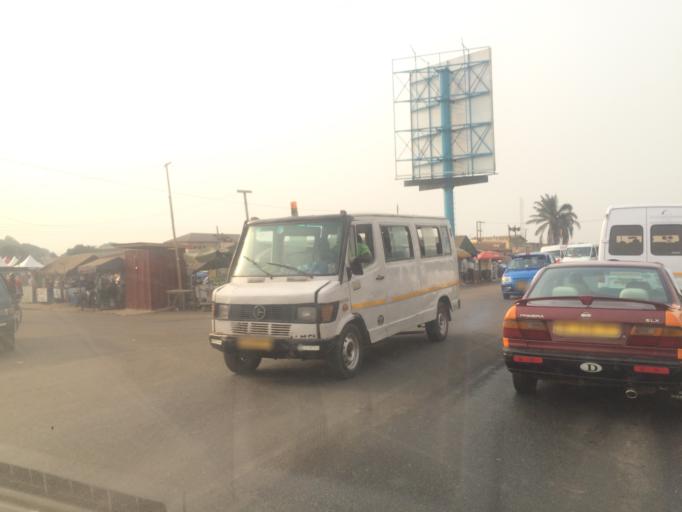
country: GH
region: Greater Accra
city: Nungua
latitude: 5.6027
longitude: -0.0793
